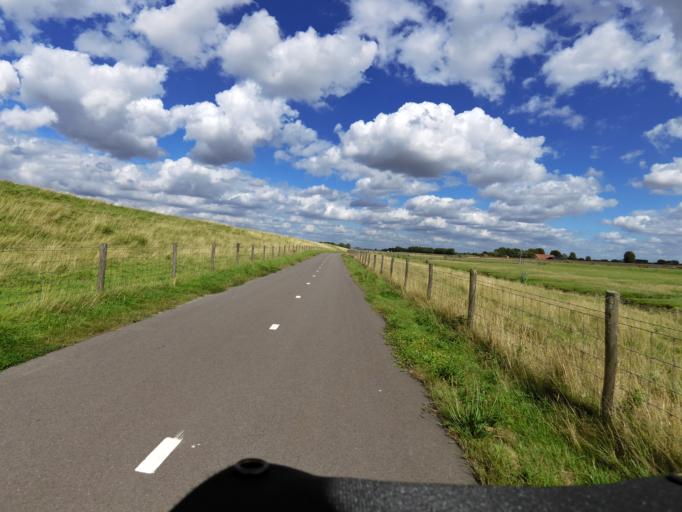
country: NL
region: South Holland
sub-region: Gemeente Oud-Beijerland
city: Oud-Beijerland
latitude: 51.8203
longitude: 4.3711
